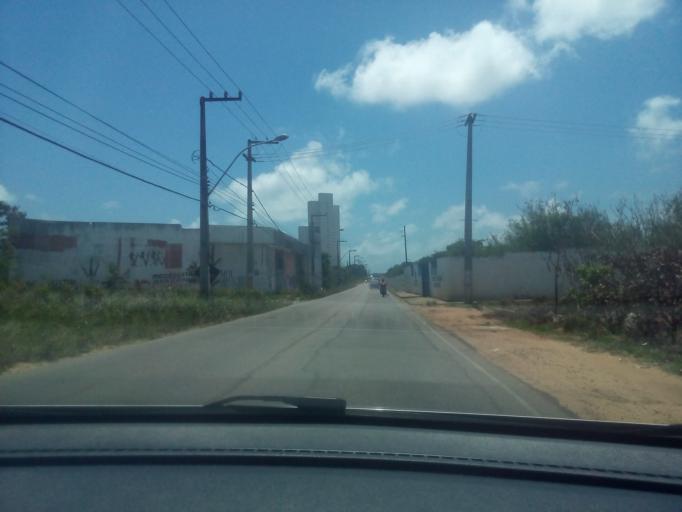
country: BR
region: Rio Grande do Norte
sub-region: Parnamirim
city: Parnamirim
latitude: -5.8877
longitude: -35.1875
